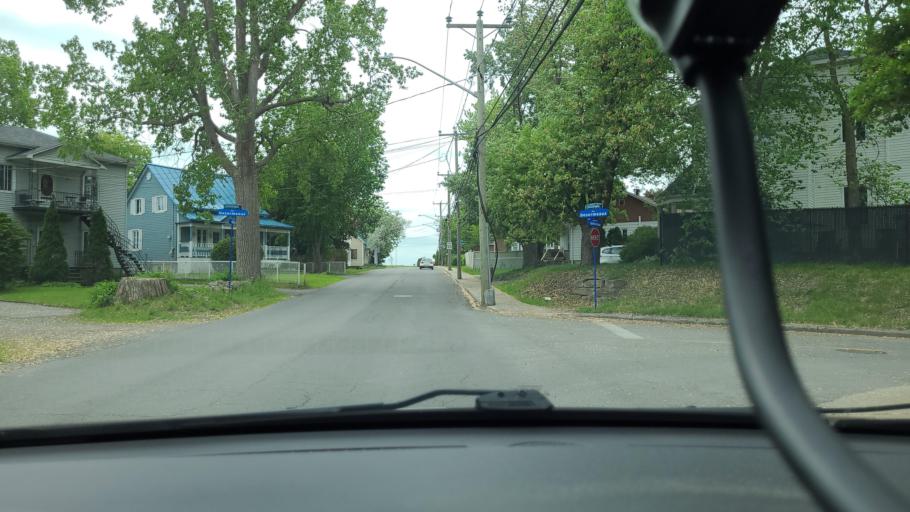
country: CA
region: Quebec
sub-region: Laurentides
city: Rosemere
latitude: 45.6031
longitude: -73.8019
